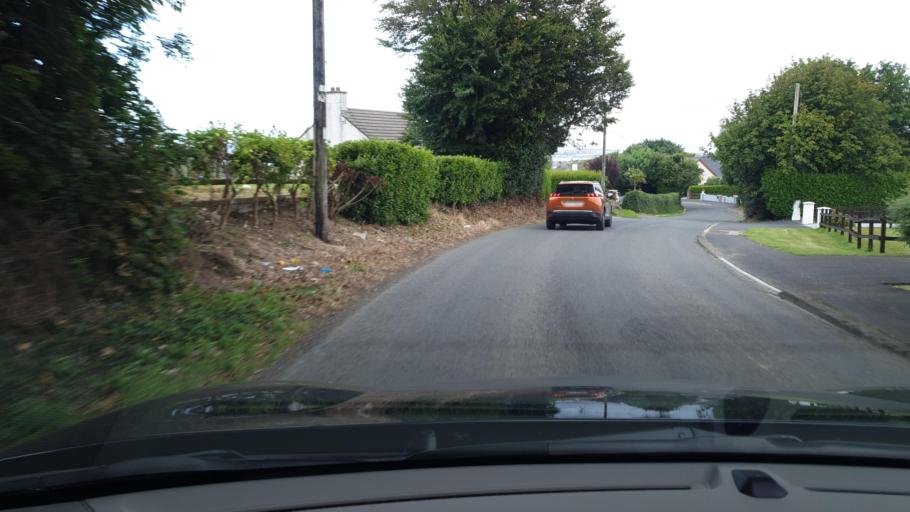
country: IE
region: Leinster
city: Balrothery
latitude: 53.5802
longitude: -6.1543
